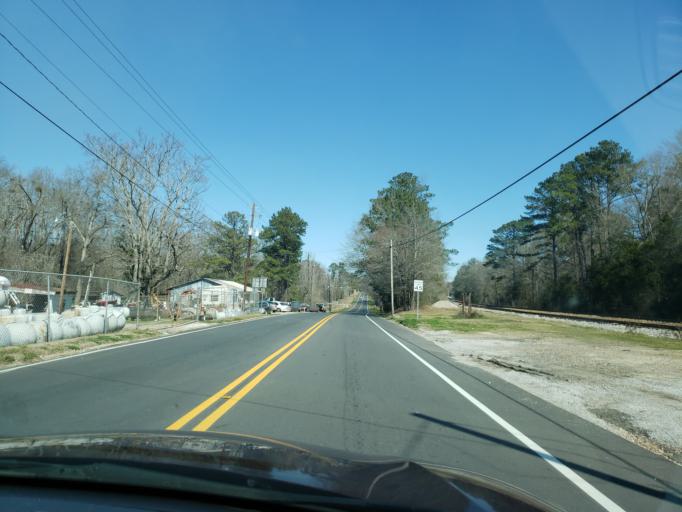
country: US
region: Alabama
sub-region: Macon County
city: Tuskegee
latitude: 32.5623
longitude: -85.6693
